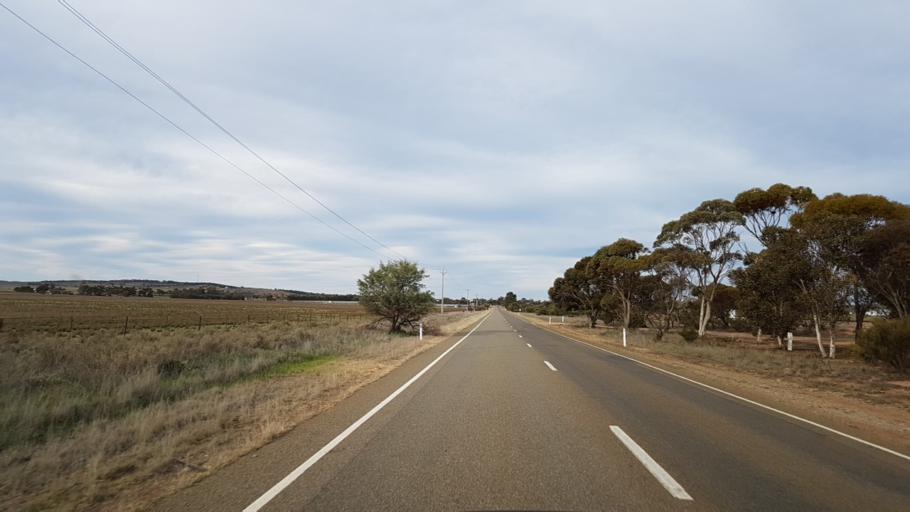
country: AU
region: South Australia
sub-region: Peterborough
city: Peterborough
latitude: -32.9841
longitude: 138.8067
